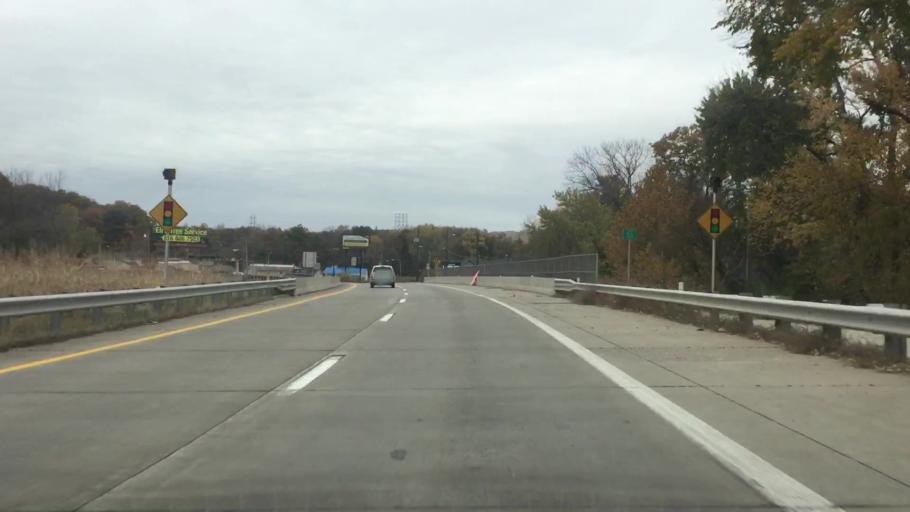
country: US
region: Missouri
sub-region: Jackson County
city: Raytown
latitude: 38.9636
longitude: -94.4261
